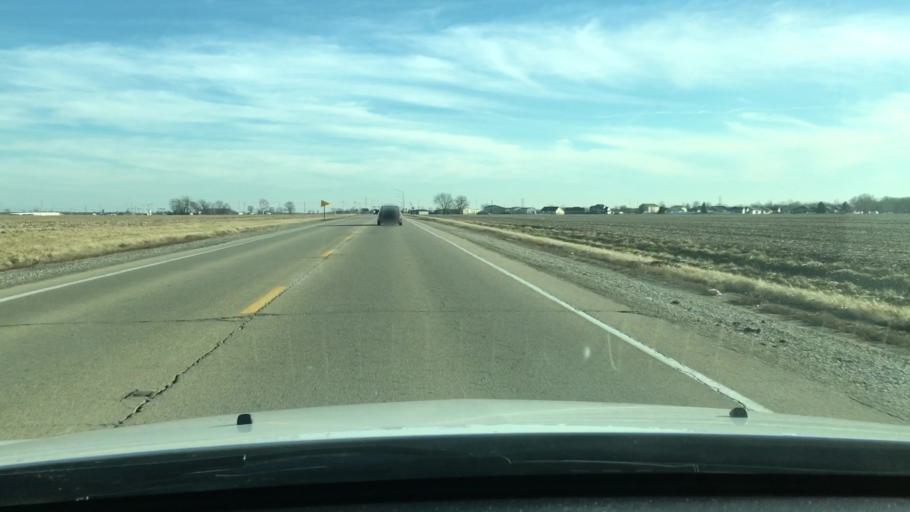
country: US
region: Illinois
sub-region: LaSalle County
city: Peru
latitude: 41.2998
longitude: -89.1069
